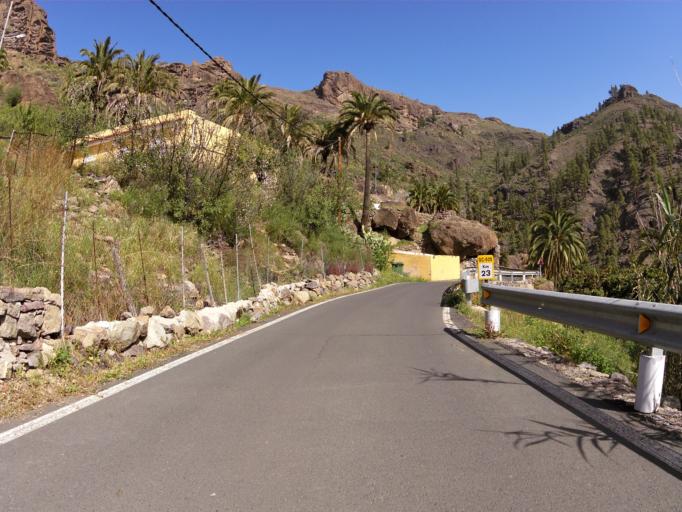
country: ES
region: Canary Islands
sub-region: Provincia de Las Palmas
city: Mogan
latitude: 27.9131
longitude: -15.6676
